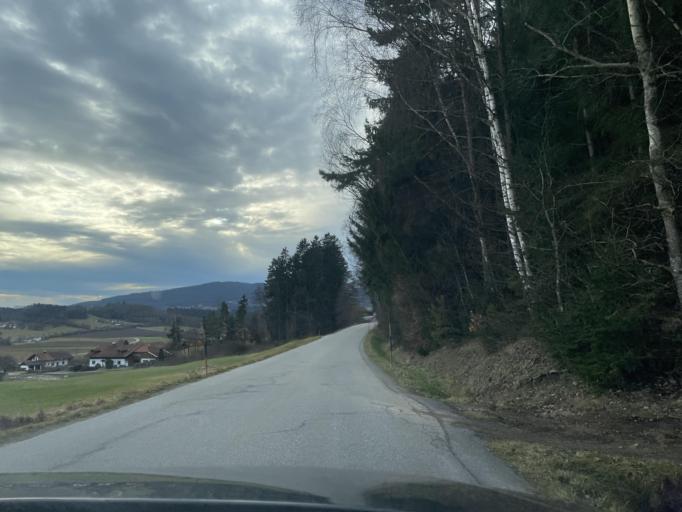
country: DE
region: Bavaria
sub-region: Lower Bavaria
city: Ruhmannsfelden
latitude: 48.9921
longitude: 13.0043
